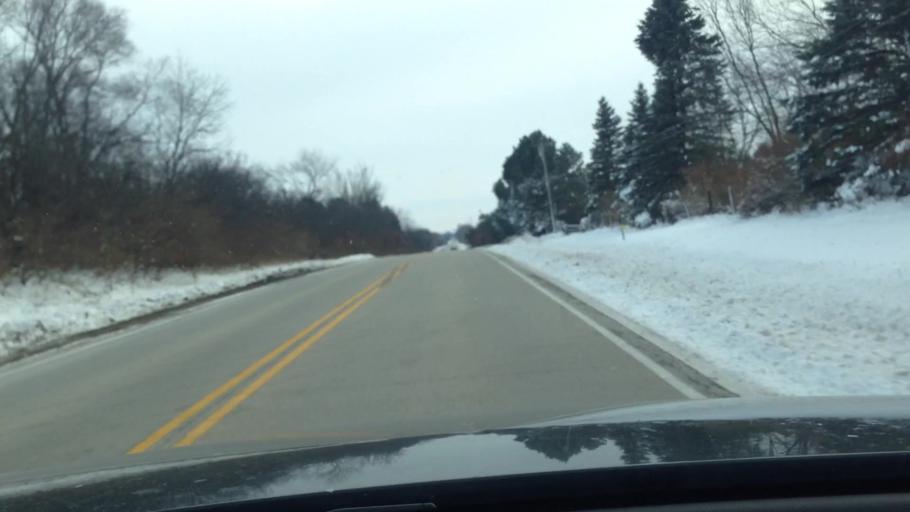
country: US
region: Illinois
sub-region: McHenry County
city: Woodstock
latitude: 42.3838
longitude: -88.4433
